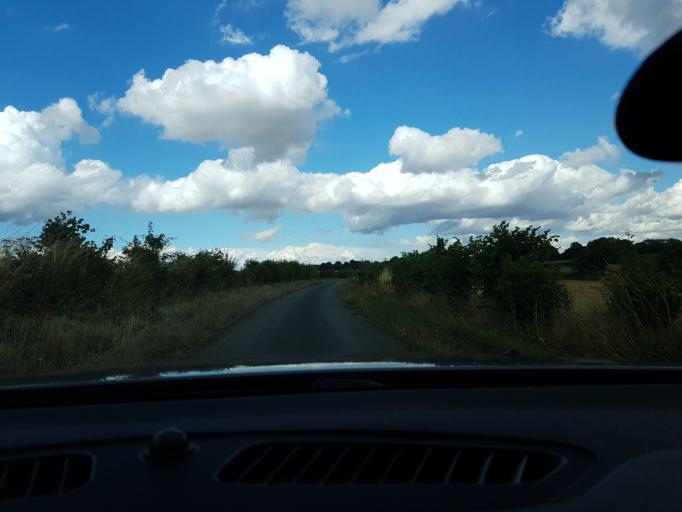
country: GB
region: England
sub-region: Wiltshire
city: Chilton Foliat
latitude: 51.4582
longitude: -1.5633
